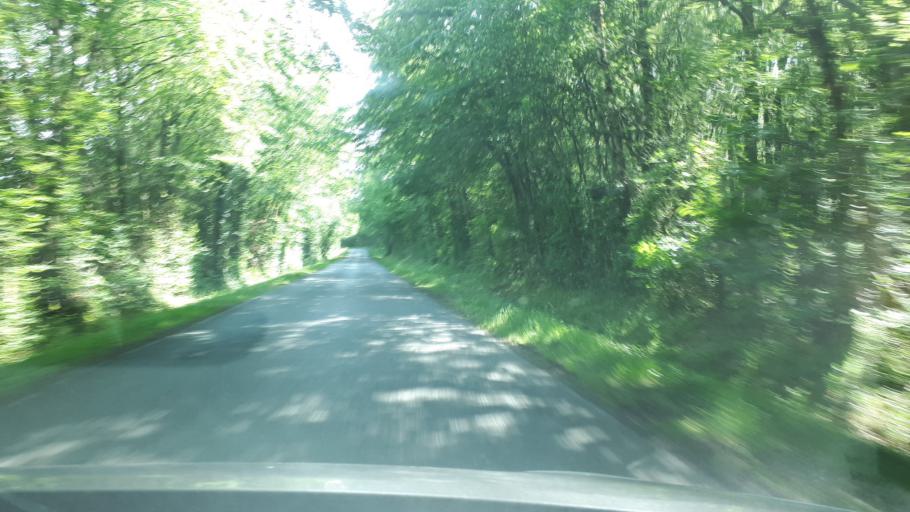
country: FR
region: Centre
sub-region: Departement du Cher
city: Henrichemont
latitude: 47.4093
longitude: 2.6048
